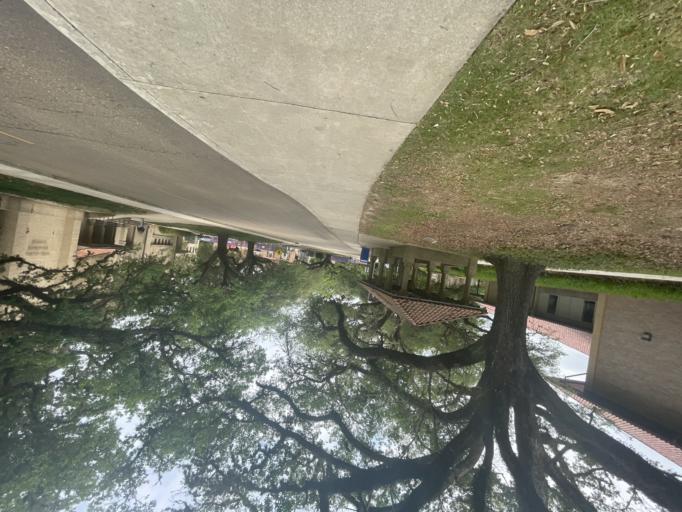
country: US
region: Louisiana
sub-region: East Baton Rouge Parish
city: Baton Rouge
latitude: 30.4113
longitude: -91.1782
